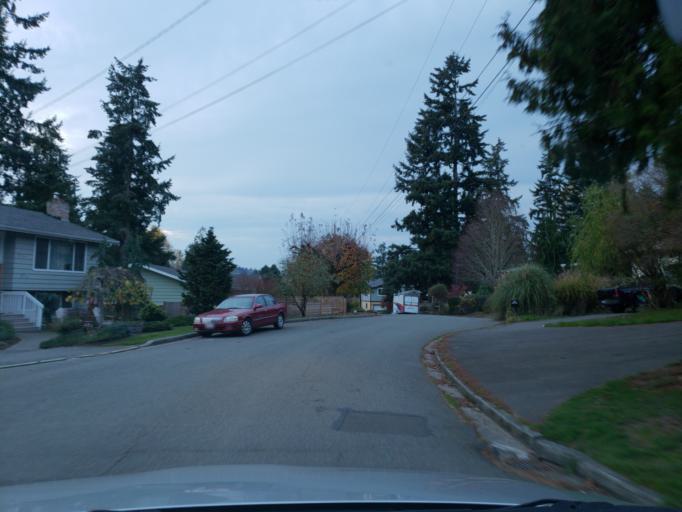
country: US
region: Washington
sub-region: King County
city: Kenmore
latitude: 47.7746
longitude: -122.2384
